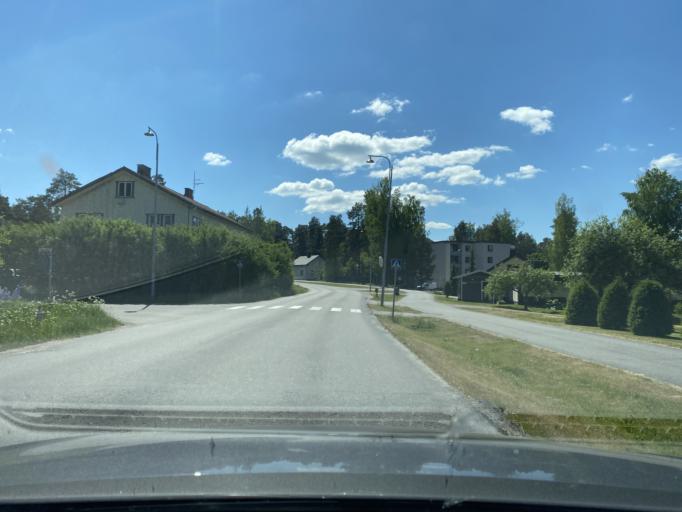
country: FI
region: Satakunta
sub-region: Rauma
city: Eura
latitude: 61.1222
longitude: 22.1595
